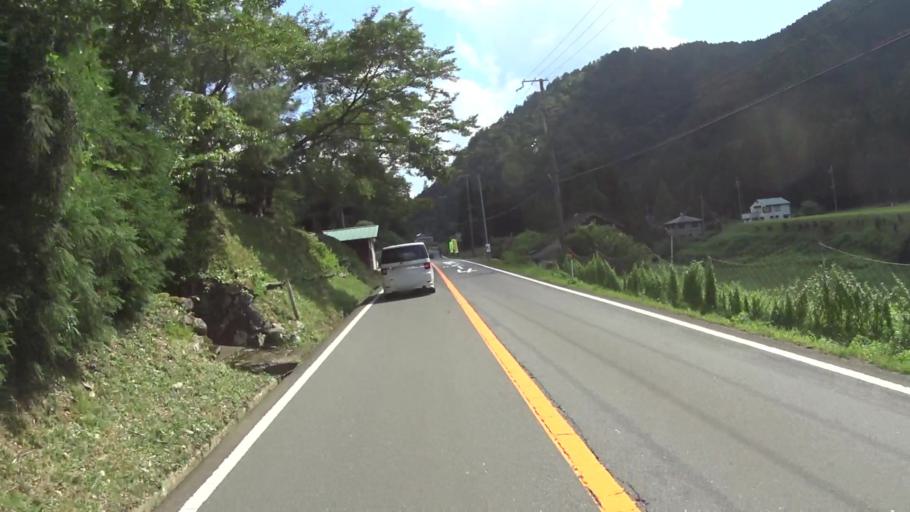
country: JP
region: Kyoto
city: Maizuru
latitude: 35.2991
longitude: 135.5570
